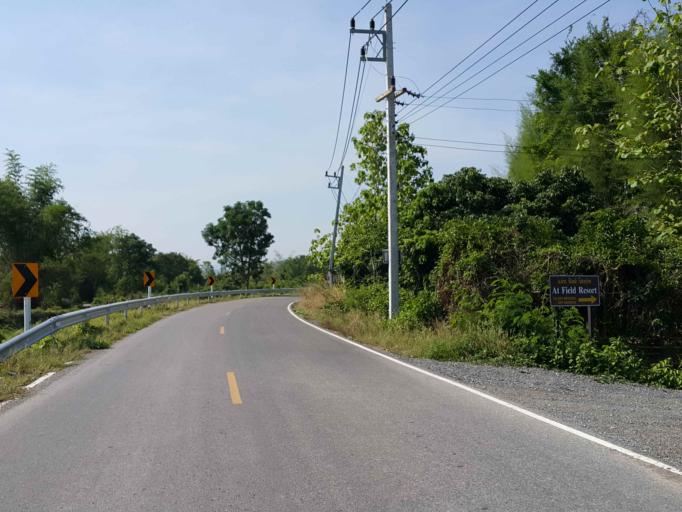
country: TH
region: Chiang Mai
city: Mae On
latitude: 18.8145
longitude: 99.1740
